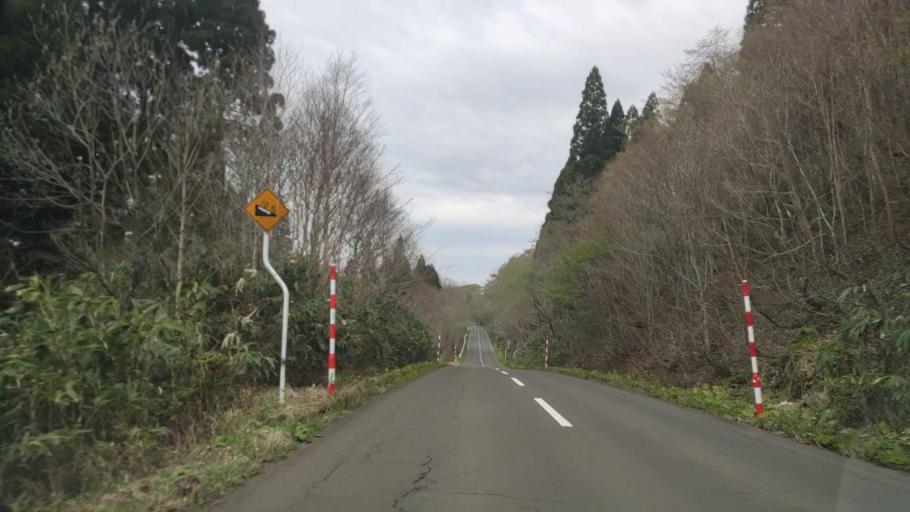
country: JP
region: Akita
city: Hanawa
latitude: 40.4084
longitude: 140.8155
